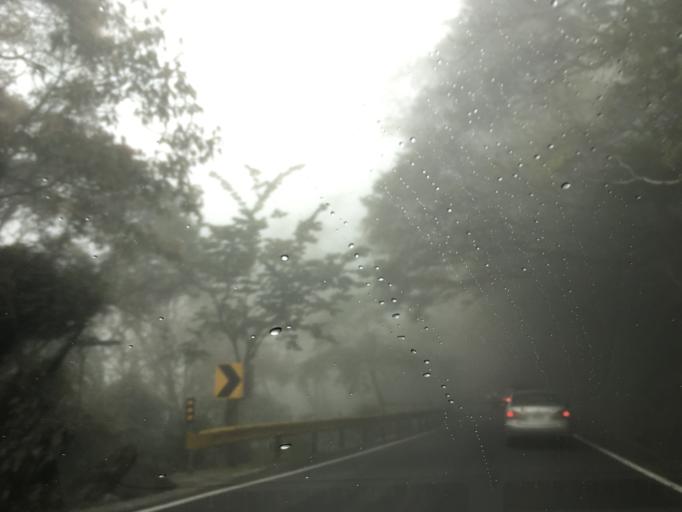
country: TW
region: Taiwan
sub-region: Hualien
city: Hualian
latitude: 24.1847
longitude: 121.4200
